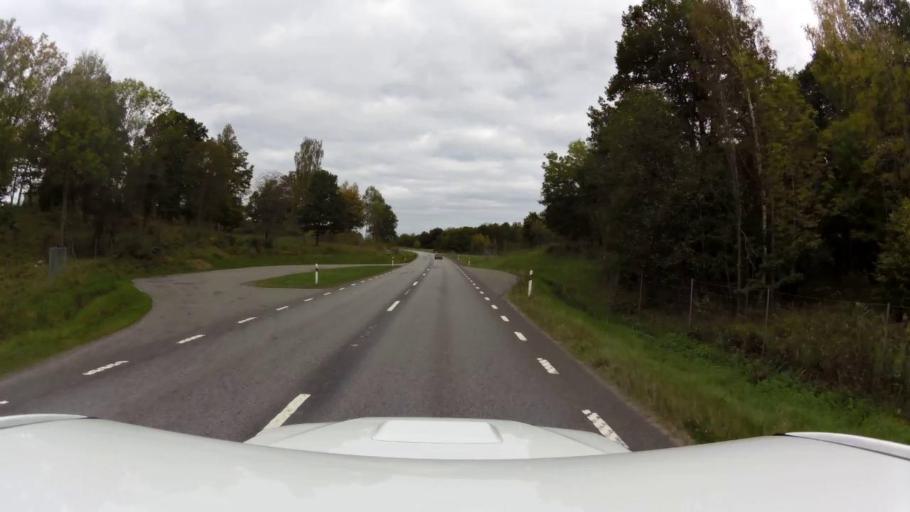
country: SE
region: OEstergoetland
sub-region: Kinda Kommun
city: Rimforsa
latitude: 58.2178
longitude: 15.6648
